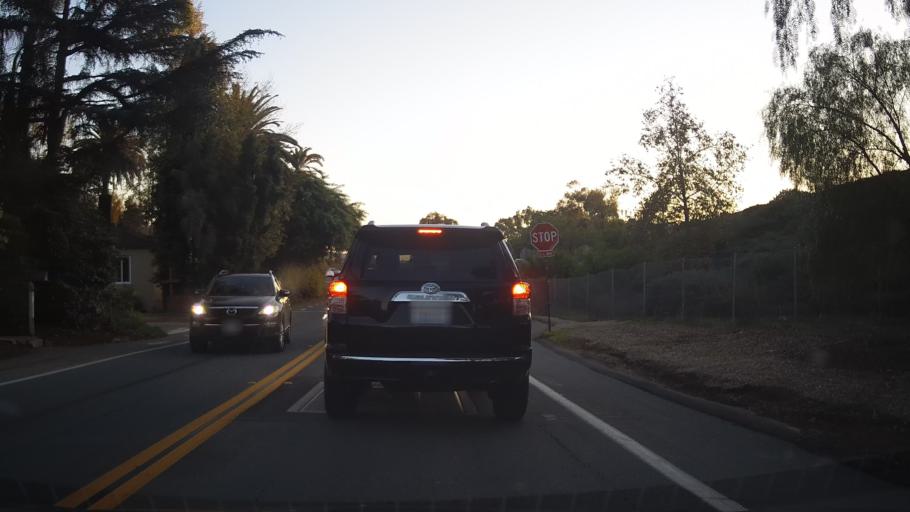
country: US
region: California
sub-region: San Diego County
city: La Mesa
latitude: 32.7700
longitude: -117.0014
